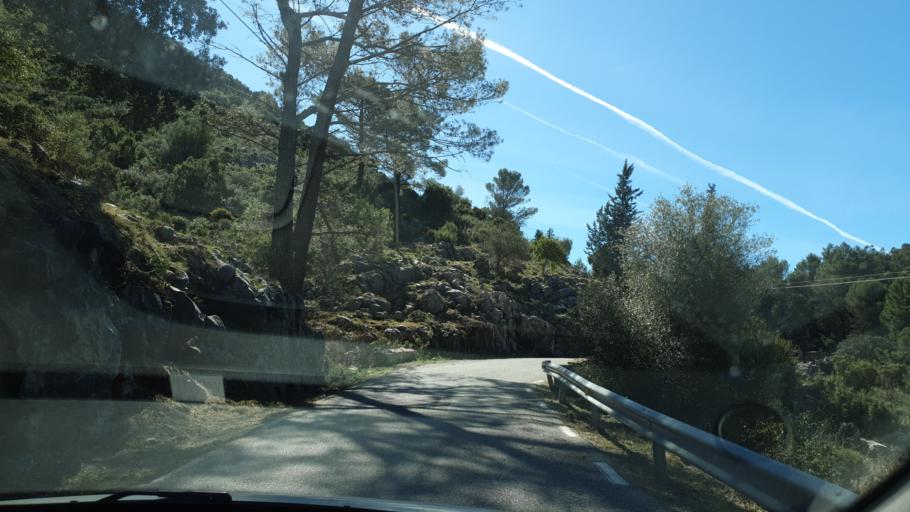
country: ES
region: Andalusia
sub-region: Provincia de Malaga
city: Ojen
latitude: 36.5821
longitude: -4.8840
